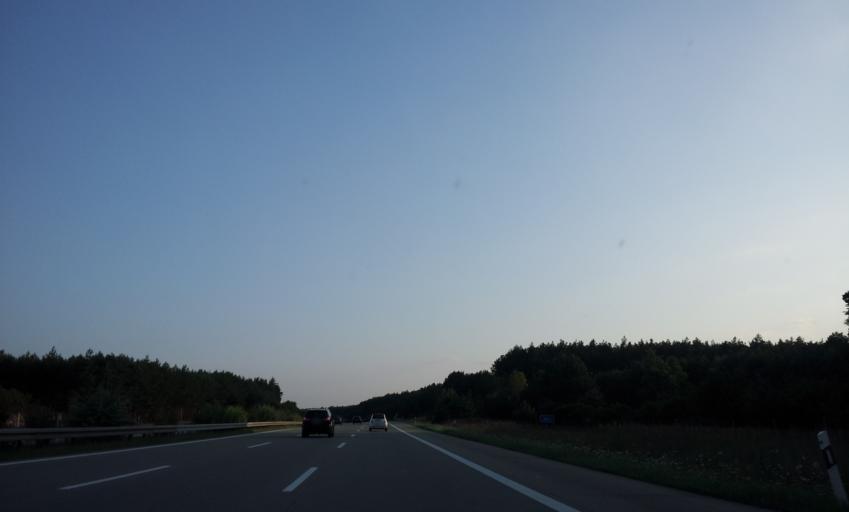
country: DE
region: Brandenburg
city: Erkner
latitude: 52.3755
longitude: 13.7720
